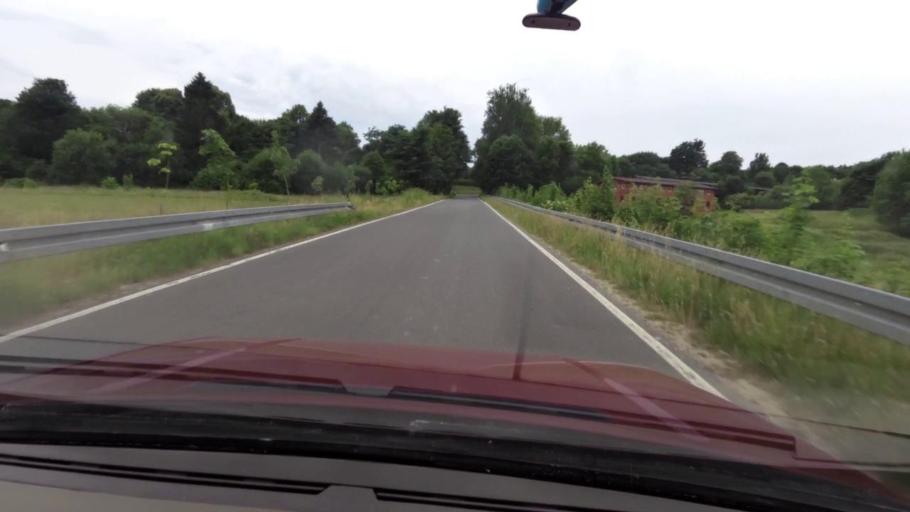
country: PL
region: West Pomeranian Voivodeship
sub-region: Powiat koszalinski
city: Polanow
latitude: 54.1603
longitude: 16.7356
